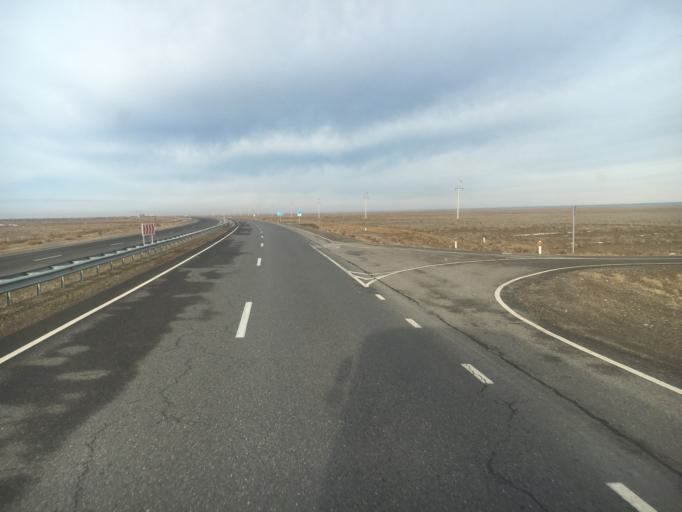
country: KZ
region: Ongtustik Qazaqstan
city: Turkestan
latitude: 43.5003
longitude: 67.8457
